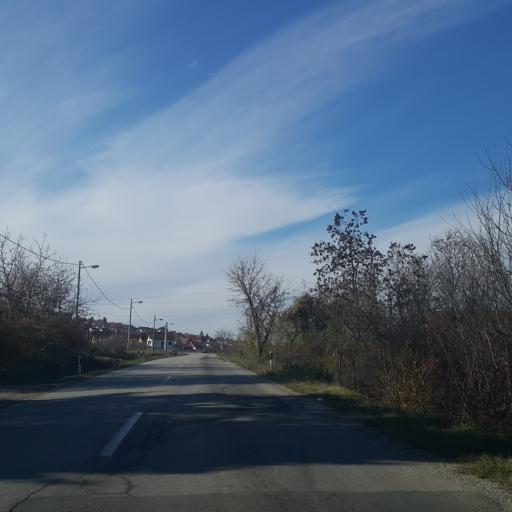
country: RS
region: Central Serbia
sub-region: Sumadijski Okrug
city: Topola
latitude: 44.2488
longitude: 20.7011
